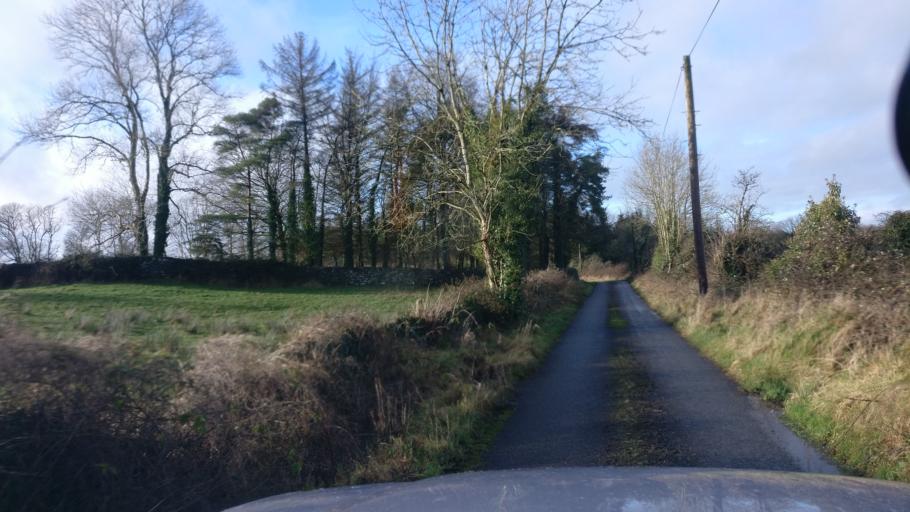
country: IE
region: Connaught
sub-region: County Galway
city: Loughrea
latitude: 53.2497
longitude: -8.6181
